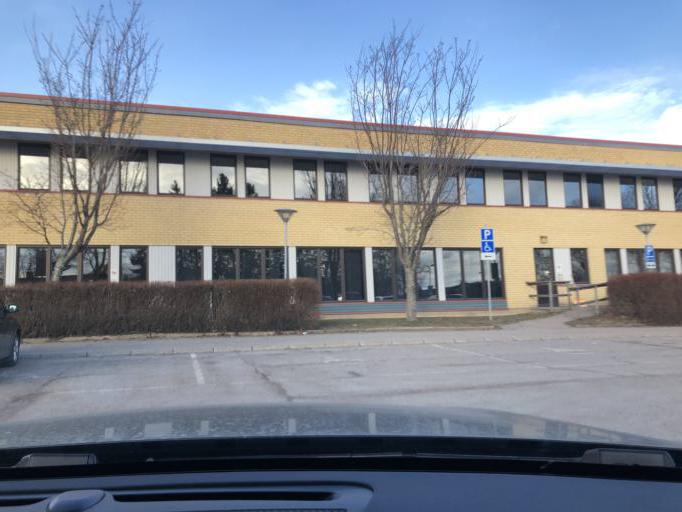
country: SE
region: Uppsala
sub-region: Tierps Kommun
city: Tierp
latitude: 60.3364
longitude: 17.5149
